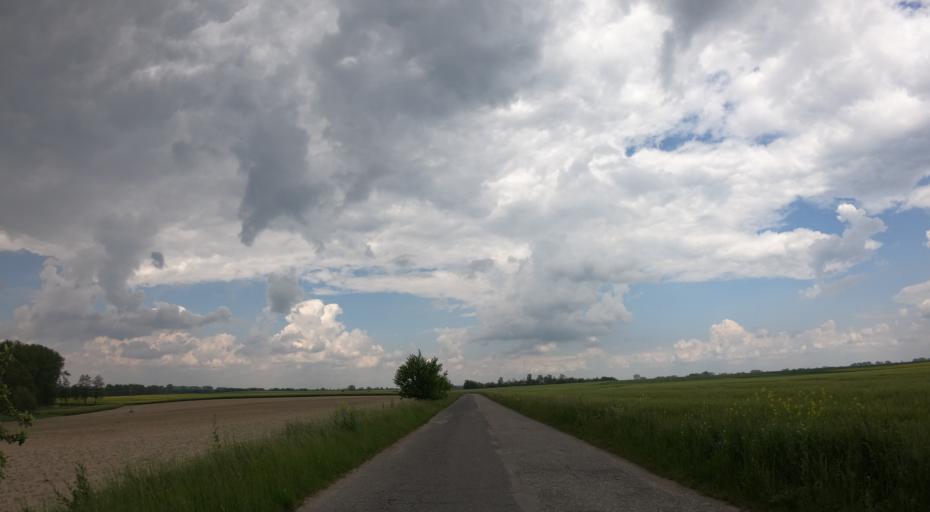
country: PL
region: West Pomeranian Voivodeship
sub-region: Powiat pyrzycki
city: Kozielice
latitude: 53.1554
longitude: 14.7948
